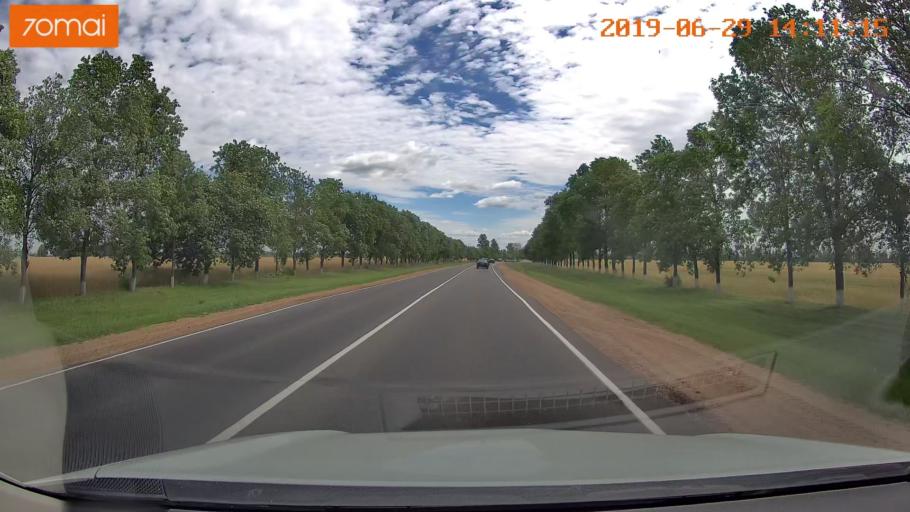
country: BY
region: Minsk
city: Salihorsk
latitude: 52.8217
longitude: 27.5015
